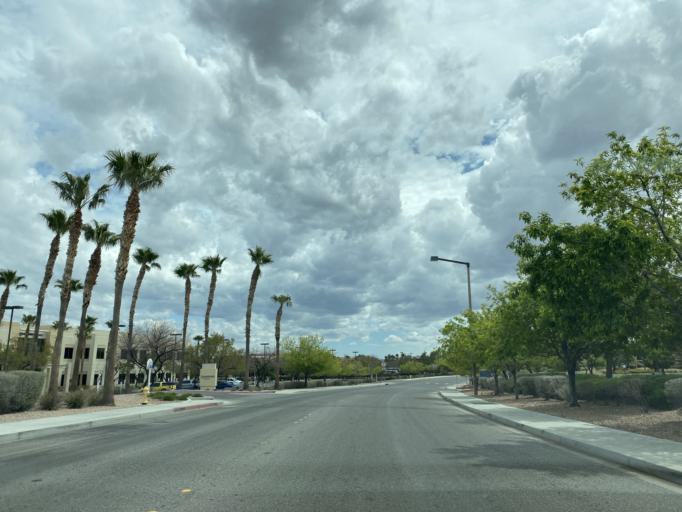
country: US
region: Nevada
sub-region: Clark County
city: Summerlin South
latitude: 36.1882
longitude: -115.3117
